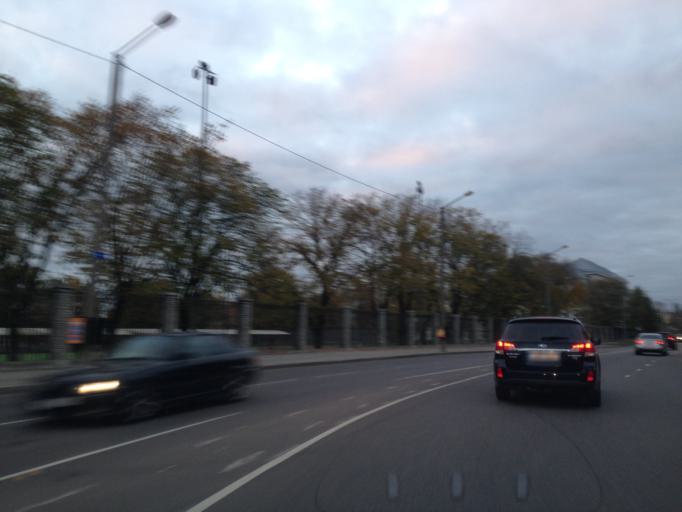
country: EE
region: Harju
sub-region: Tallinna linn
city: Tallinn
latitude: 59.4265
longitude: 24.8006
